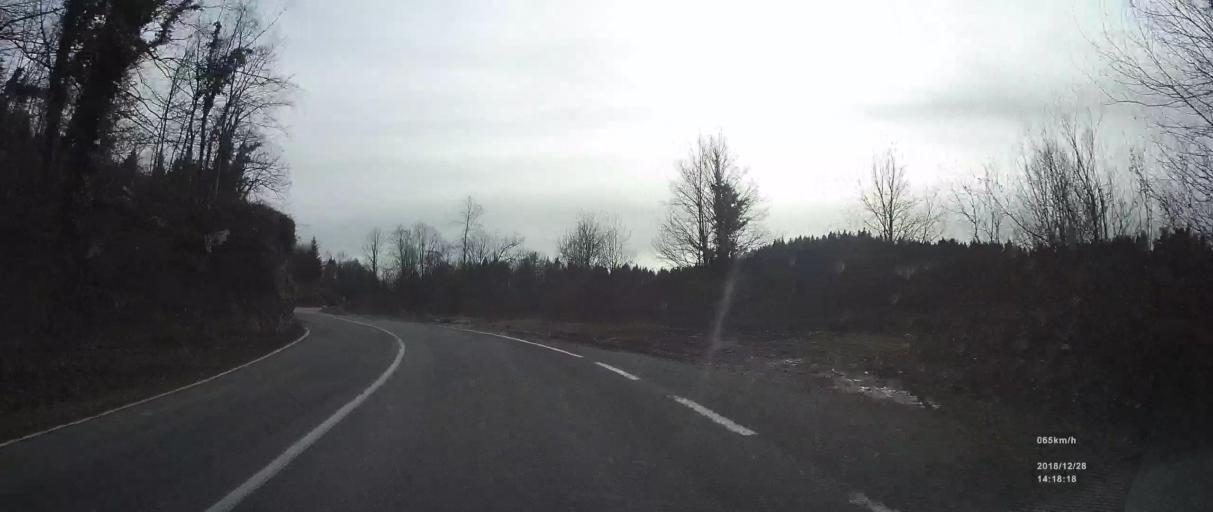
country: HR
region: Primorsko-Goranska
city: Vrbovsko
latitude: 45.4142
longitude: 15.0593
